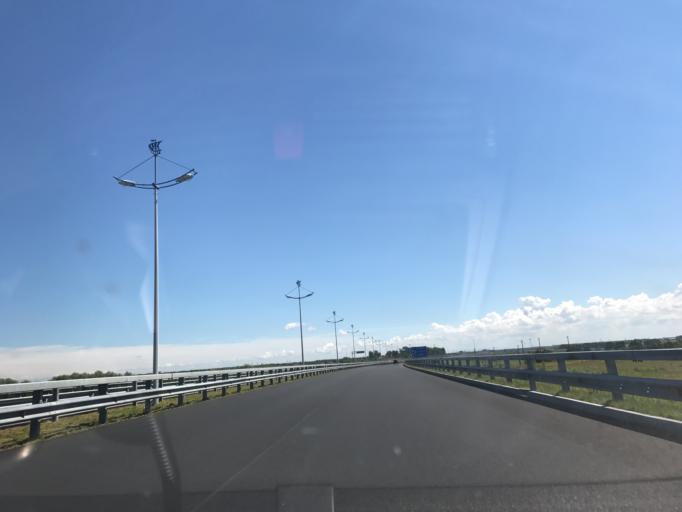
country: RU
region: Kaliningrad
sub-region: Zelenogradskiy Rayon
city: Zelenogradsk
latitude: 54.9158
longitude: 20.4842
